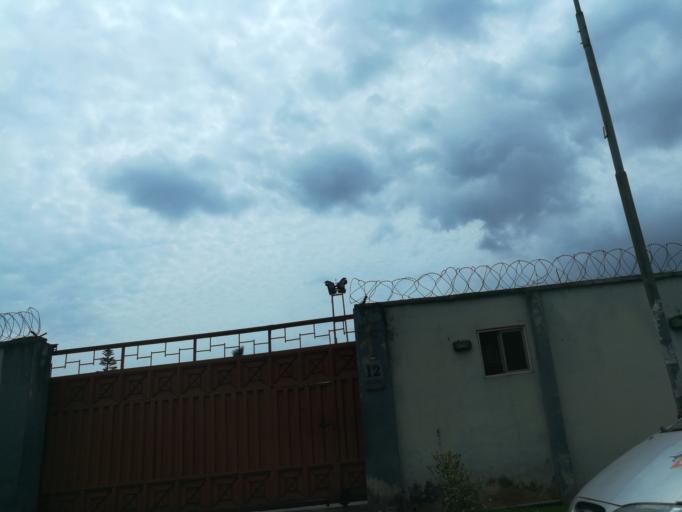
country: NG
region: Lagos
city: Ojota
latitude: 6.5773
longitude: 3.3684
